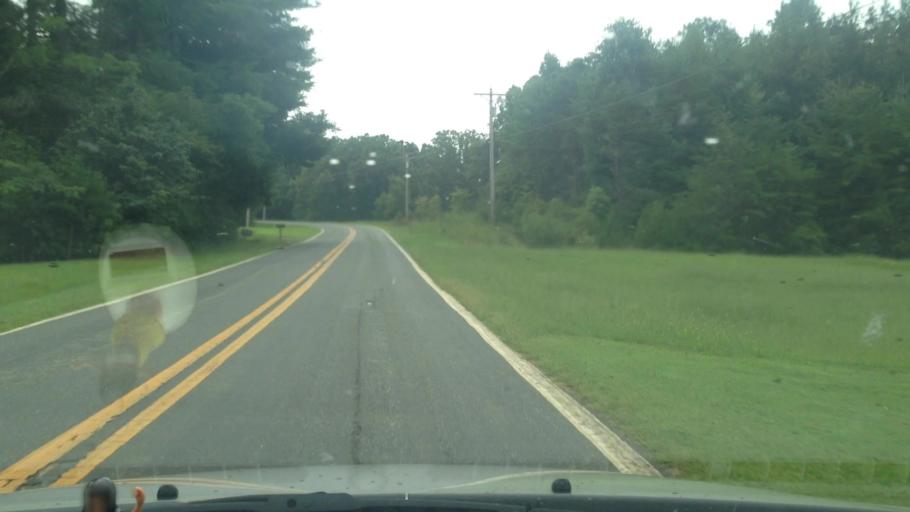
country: US
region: North Carolina
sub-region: Stokes County
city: Danbury
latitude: 36.3922
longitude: -80.1384
